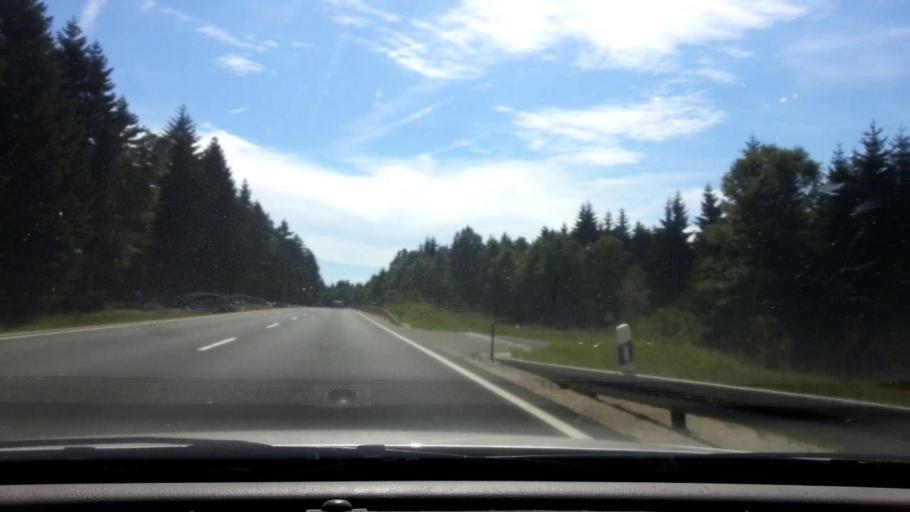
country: DE
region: Bavaria
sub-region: Upper Franconia
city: Fichtelberg
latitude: 50.0183
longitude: 11.8762
